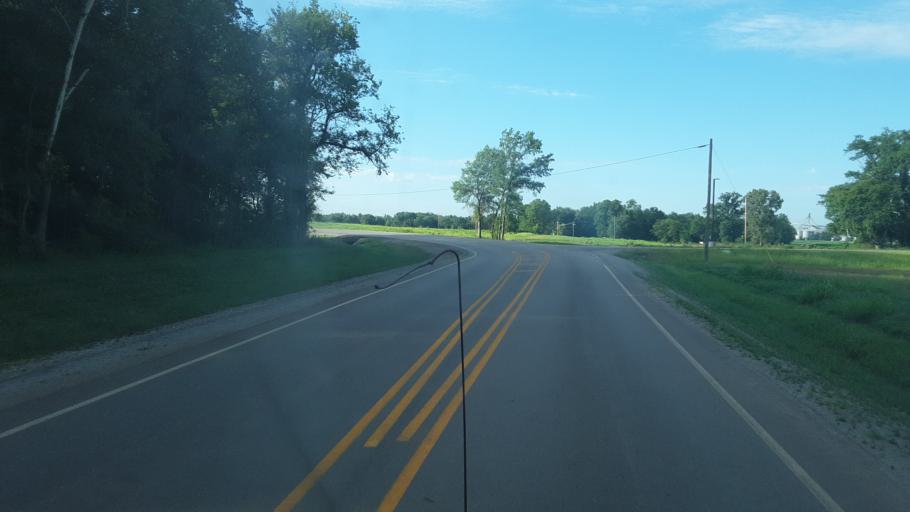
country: US
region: Kentucky
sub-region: Todd County
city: Guthrie
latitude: 36.6656
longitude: -87.1699
